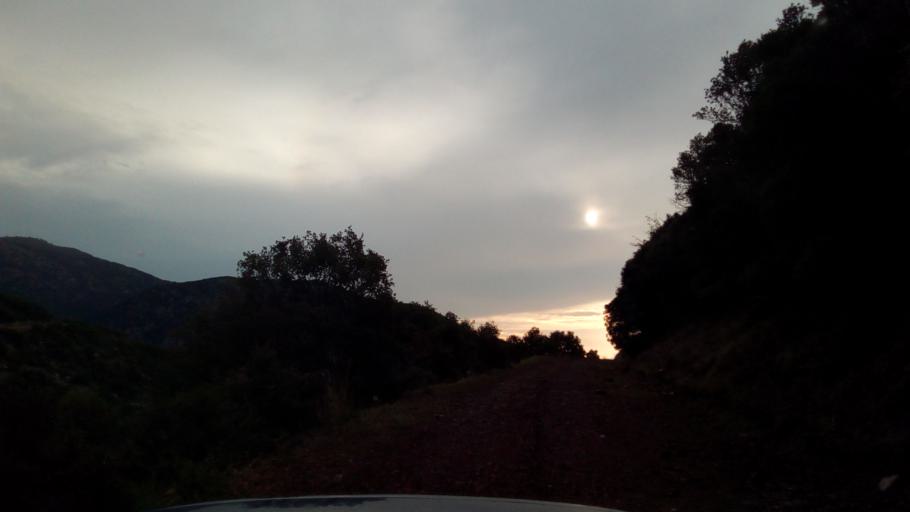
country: GR
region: West Greece
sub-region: Nomos Achaias
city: Kamarai
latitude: 38.4141
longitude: 22.0479
